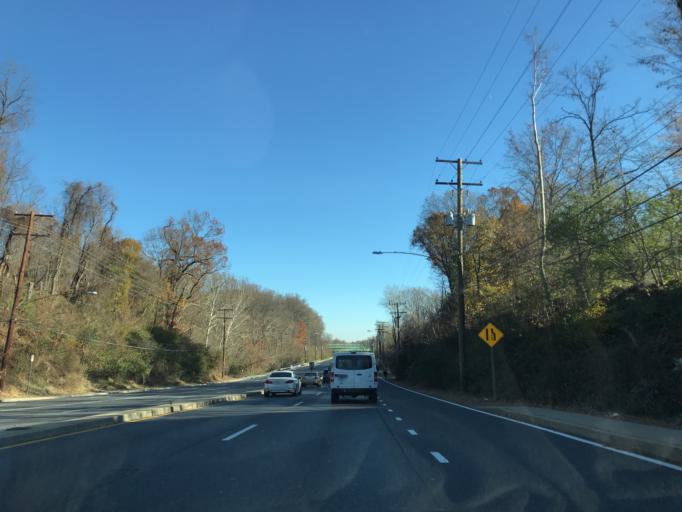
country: US
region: Maryland
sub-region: Montgomery County
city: North Bethesda
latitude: 39.0731
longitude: -77.1114
